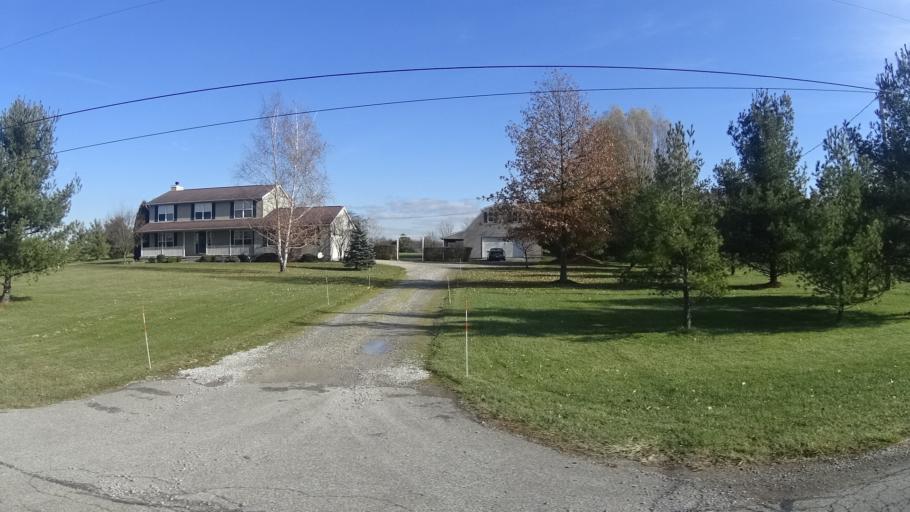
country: US
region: Ohio
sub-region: Lorain County
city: Eaton Estates
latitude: 41.3337
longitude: -81.9906
